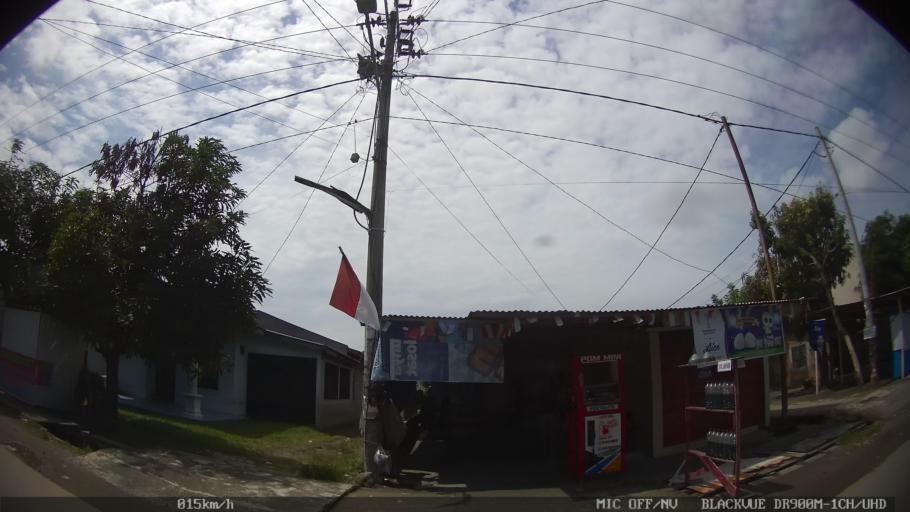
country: ID
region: North Sumatra
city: Medan
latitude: 3.5912
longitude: 98.7547
